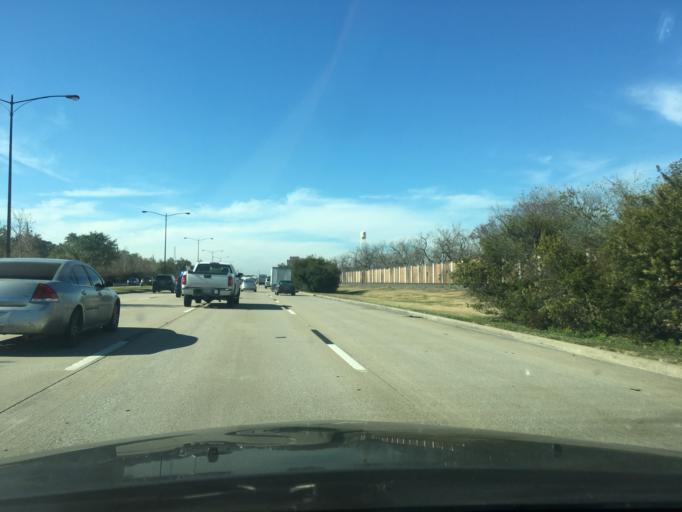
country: US
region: Texas
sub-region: Fort Bend County
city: Sugar Land
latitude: 29.6222
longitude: -95.6247
